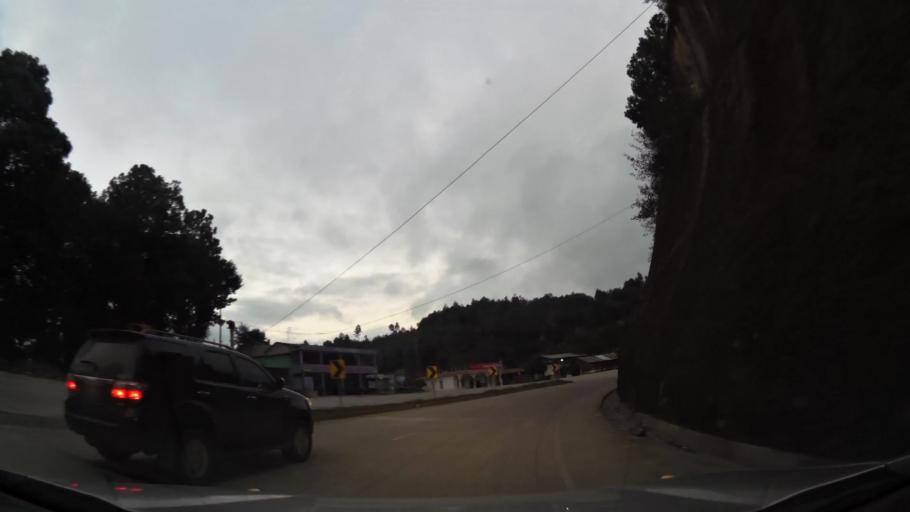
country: GT
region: Chimaltenango
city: Santa Apolonia
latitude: 14.8468
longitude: -91.0438
